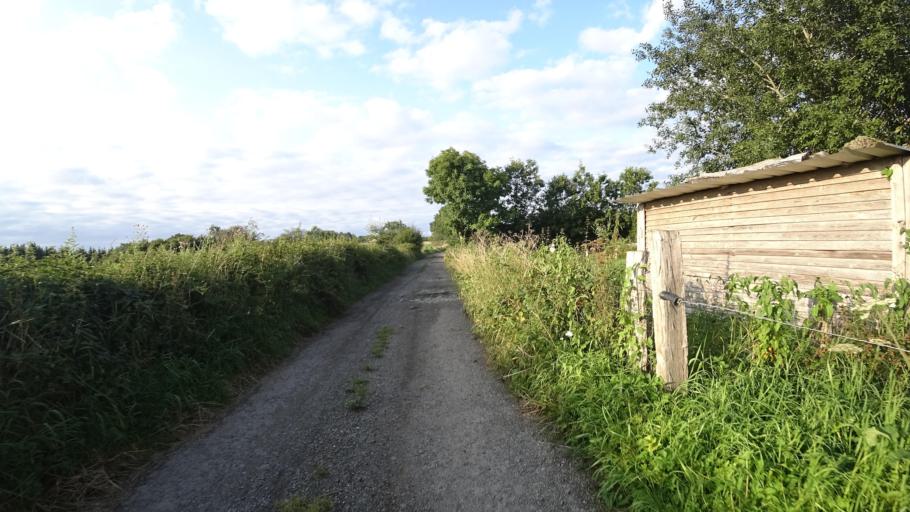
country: BE
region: Wallonia
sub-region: Province du Luxembourg
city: Neufchateau
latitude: 49.8586
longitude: 5.3688
